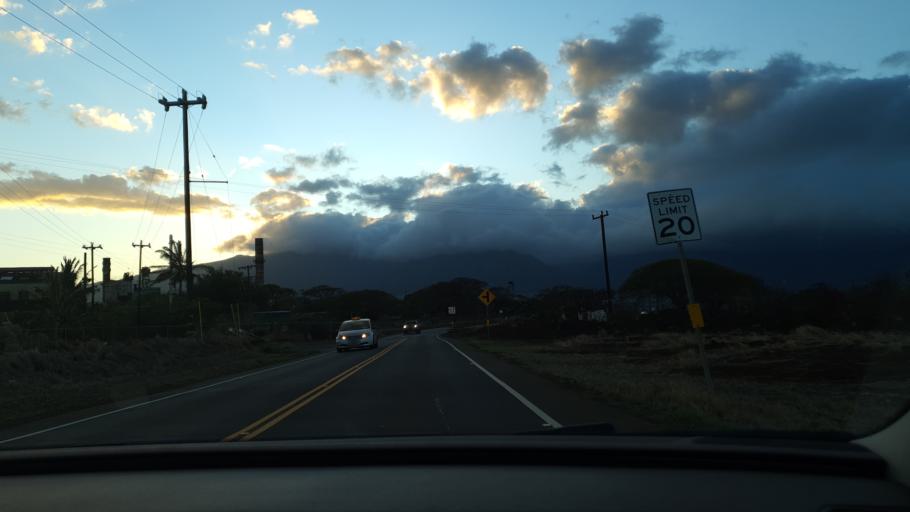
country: US
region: Hawaii
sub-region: Maui County
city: Kahului
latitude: 20.8692
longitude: -156.4505
